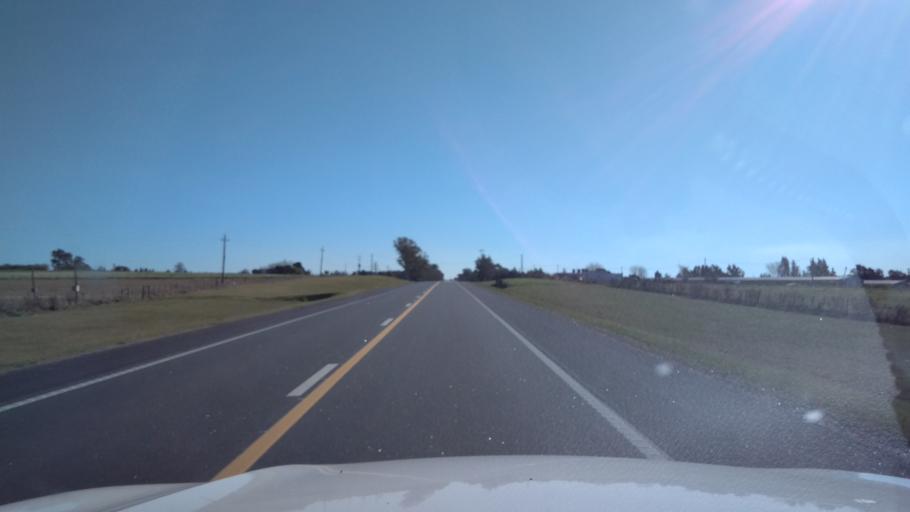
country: UY
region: Canelones
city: Santa Rosa
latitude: -34.5257
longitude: -55.9657
